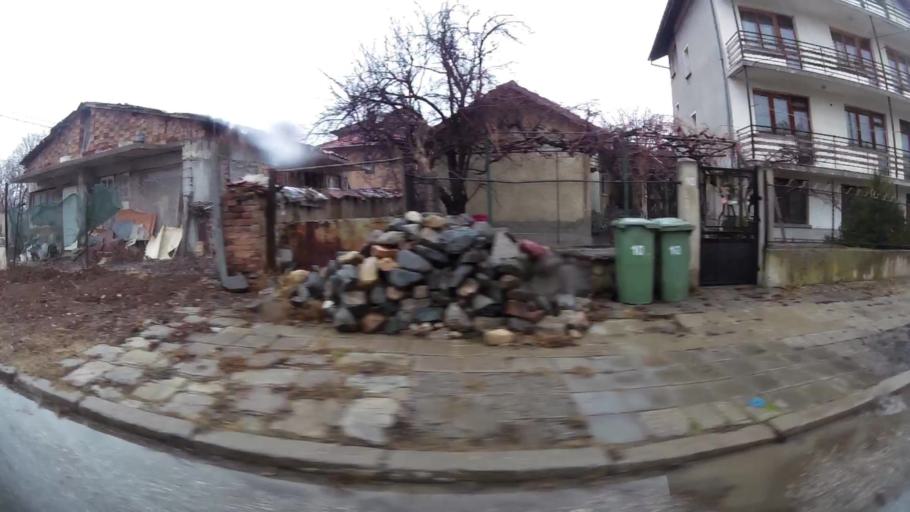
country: BG
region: Sofia-Capital
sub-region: Stolichna Obshtina
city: Sofia
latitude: 42.6313
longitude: 23.4044
